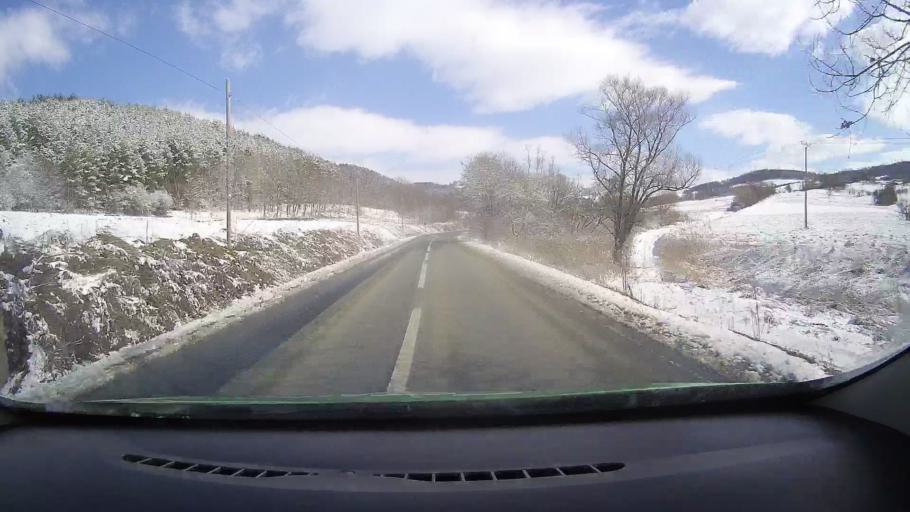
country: RO
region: Sibiu
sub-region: Comuna Barghis
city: Barghis
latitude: 45.9854
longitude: 24.4985
